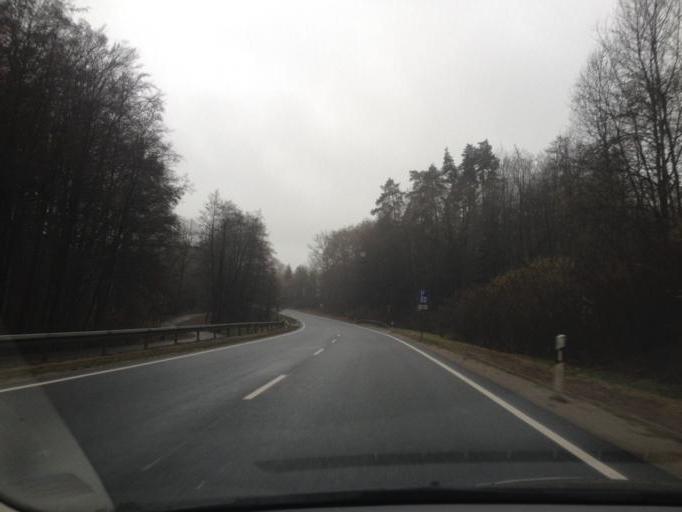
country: DE
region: Bavaria
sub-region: Regierungsbezirk Mittelfranken
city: Heroldsberg
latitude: 49.5500
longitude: 11.1648
